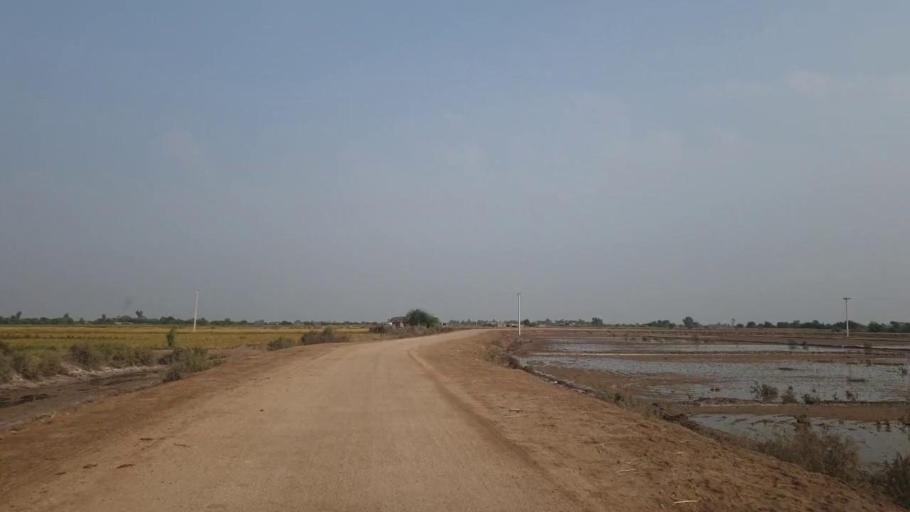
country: PK
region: Sindh
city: Badin
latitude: 24.6002
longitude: 68.6992
